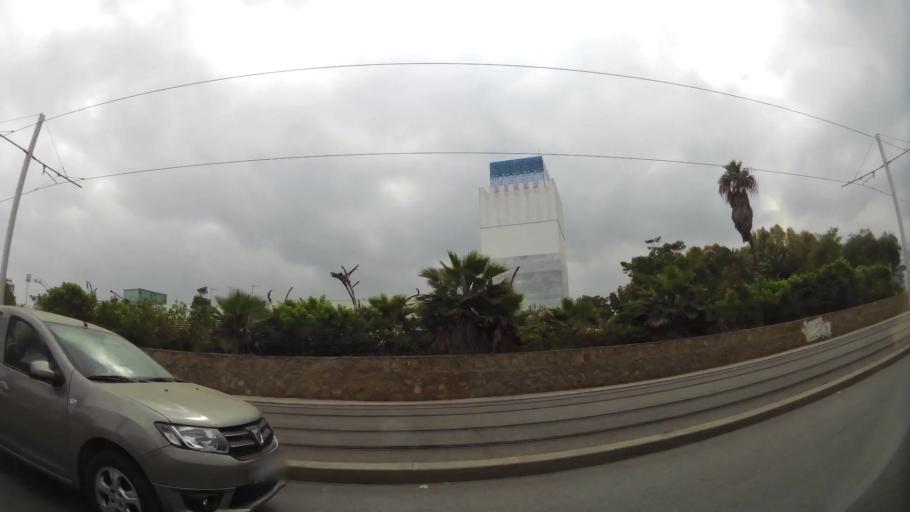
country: MA
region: Rabat-Sale-Zemmour-Zaer
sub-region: Rabat
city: Rabat
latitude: 34.0076
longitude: -6.8439
